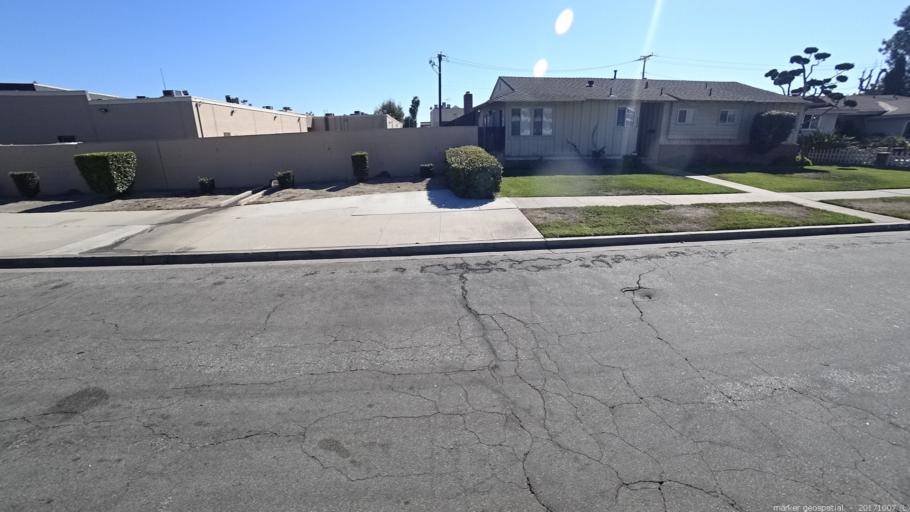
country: US
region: California
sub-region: Orange County
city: Stanton
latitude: 33.7753
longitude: -117.9774
